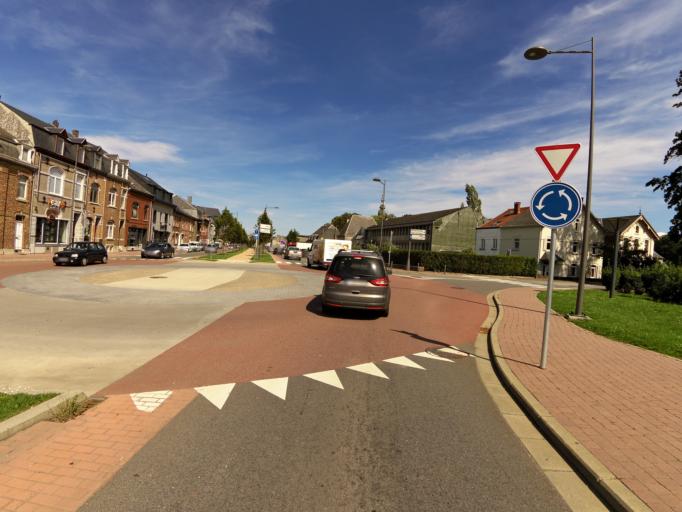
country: BE
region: Wallonia
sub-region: Province du Luxembourg
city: Marche-en-Famenne
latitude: 50.2266
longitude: 5.3405
